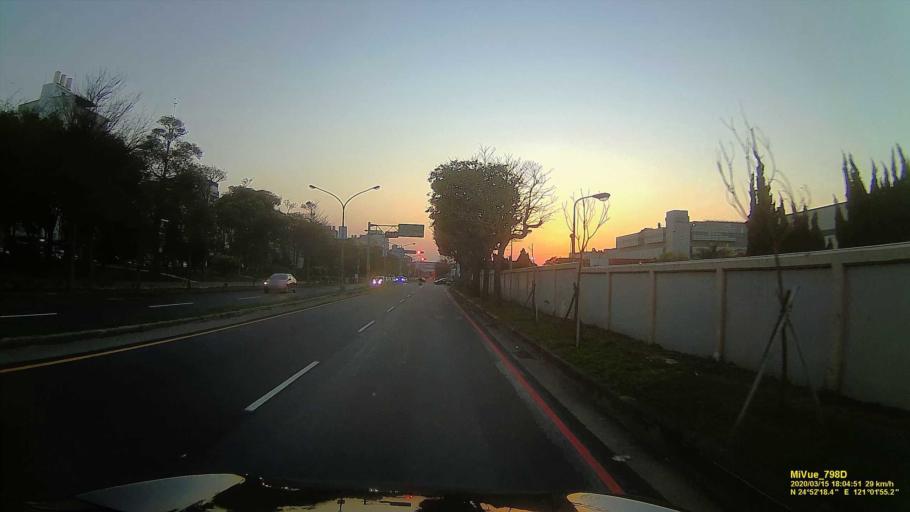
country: TW
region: Taiwan
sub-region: Hsinchu
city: Zhubei
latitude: 24.8717
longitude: 121.0318
